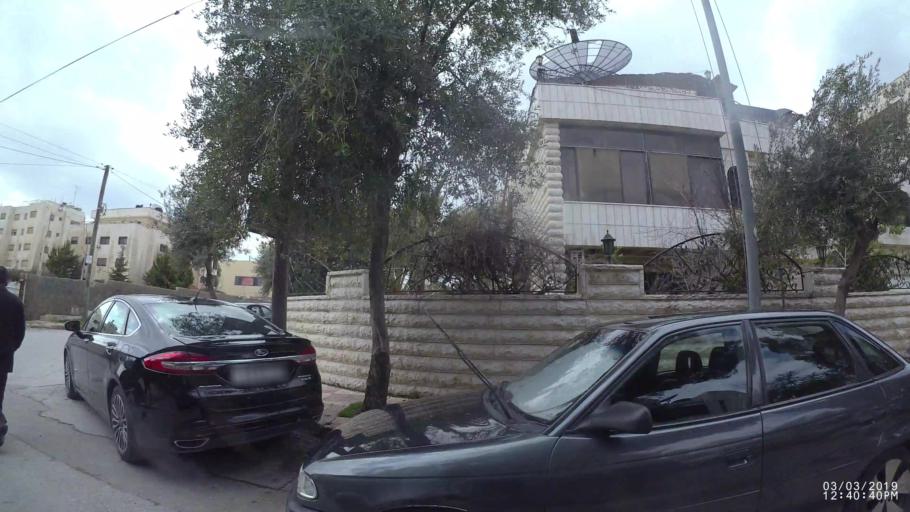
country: JO
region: Amman
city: Amman
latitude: 31.9714
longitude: 35.8985
